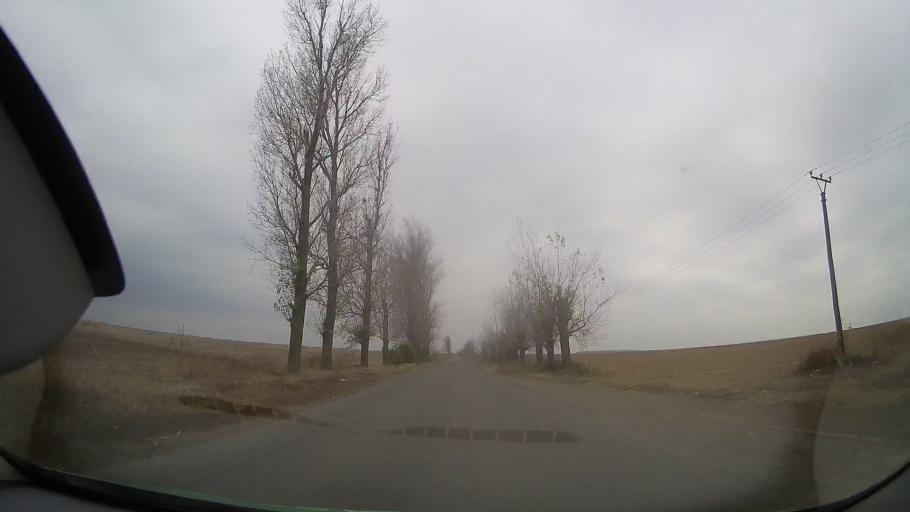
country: RO
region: Buzau
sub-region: Comuna Scutelnici
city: Scutelnici
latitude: 44.8784
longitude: 26.9457
